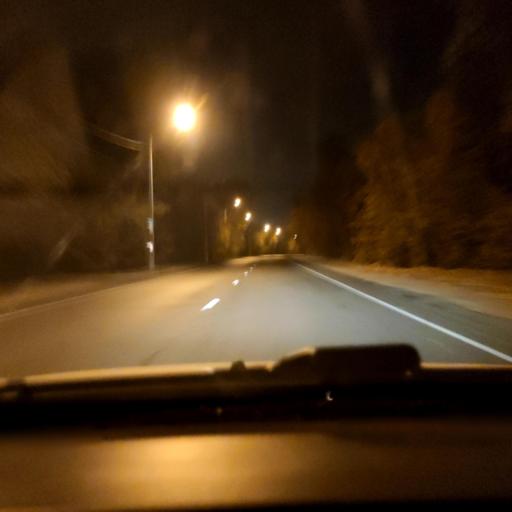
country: RU
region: Voronezj
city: Voronezh
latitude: 51.5987
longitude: 39.1770
